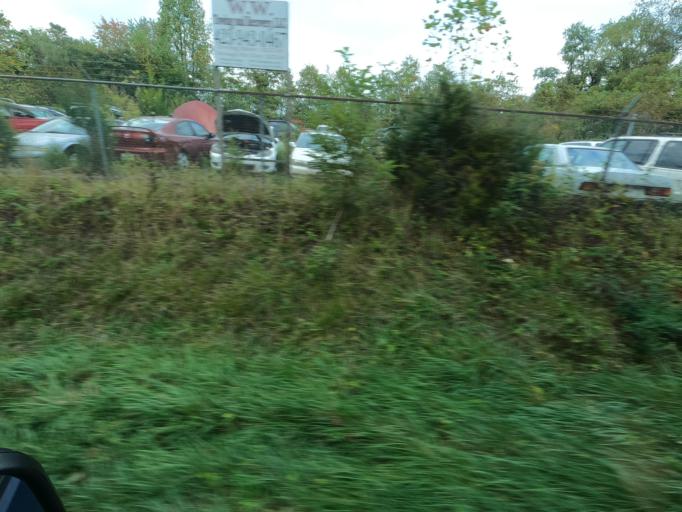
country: US
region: Tennessee
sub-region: Carter County
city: Central
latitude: 36.3262
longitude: -82.2903
